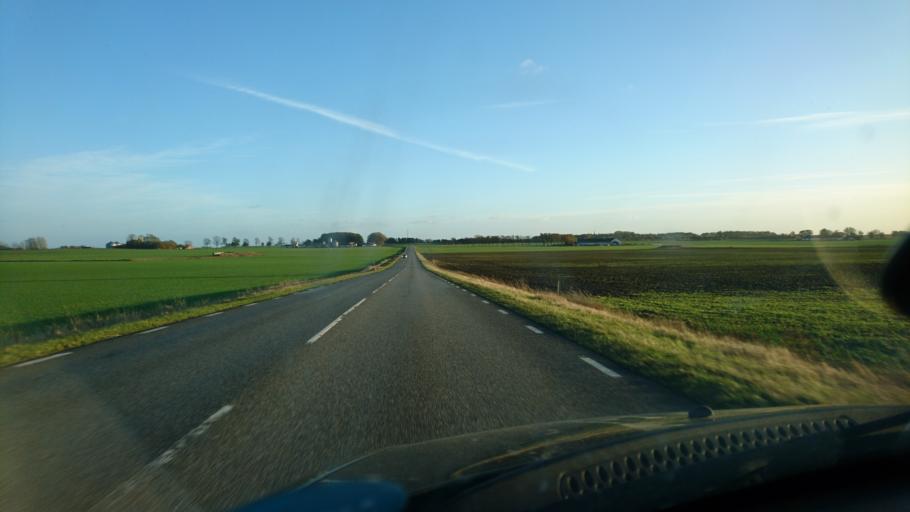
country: SE
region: Skane
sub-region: Simrishamns Kommun
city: Simrishamn
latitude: 55.4757
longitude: 14.1745
